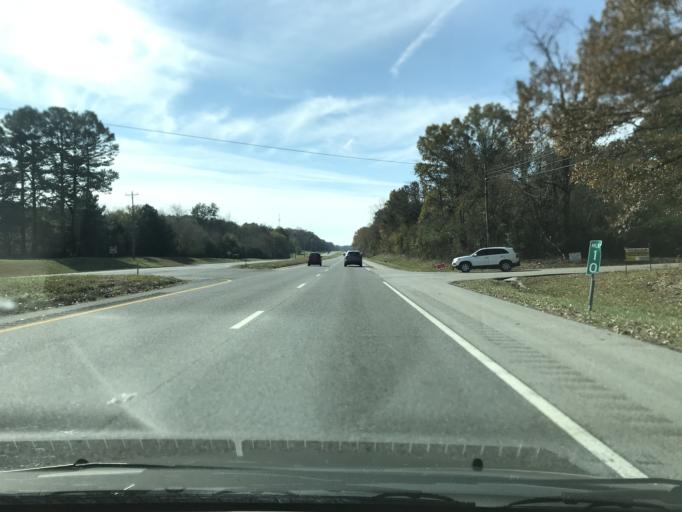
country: US
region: Tennessee
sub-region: Coffee County
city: Manchester
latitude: 35.4267
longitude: -86.1095
